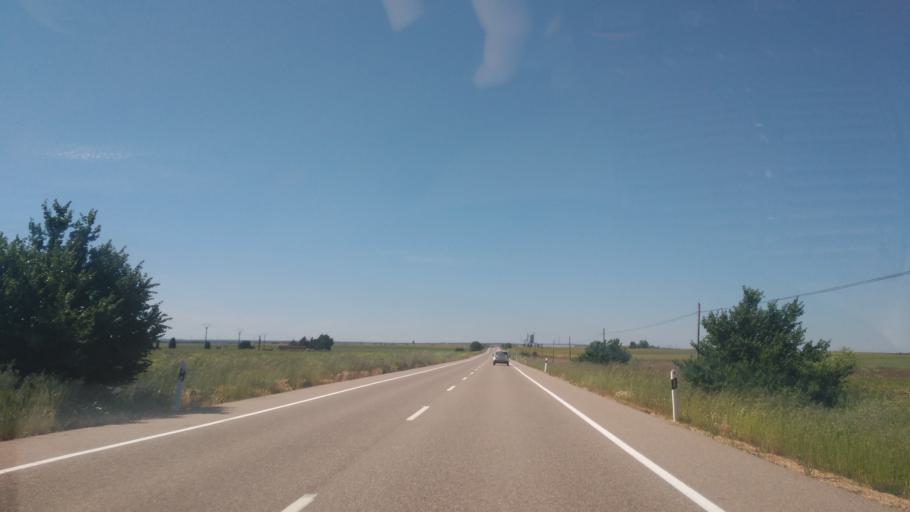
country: ES
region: Castille and Leon
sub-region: Provincia de Salamanca
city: Calzada de Valdunciel
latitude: 41.0727
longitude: -5.6908
